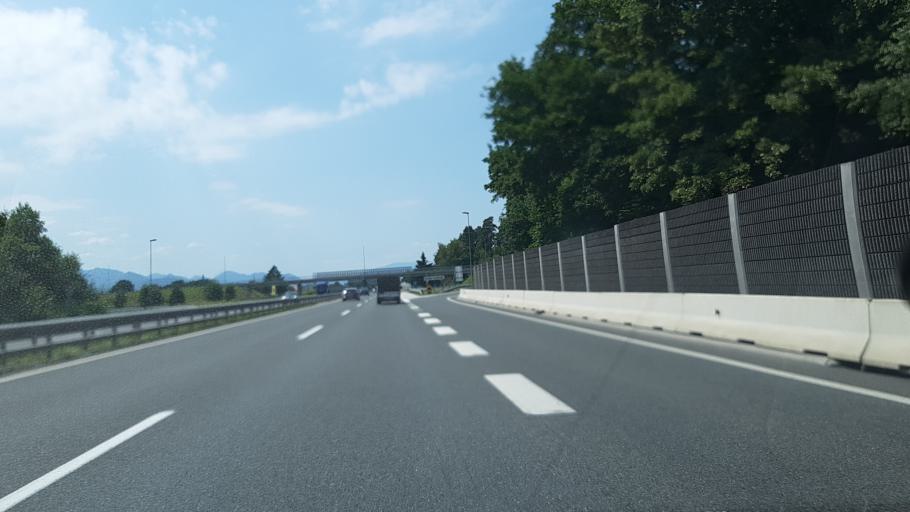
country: SI
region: Celje
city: Ljubecna
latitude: 46.2546
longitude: 15.3141
